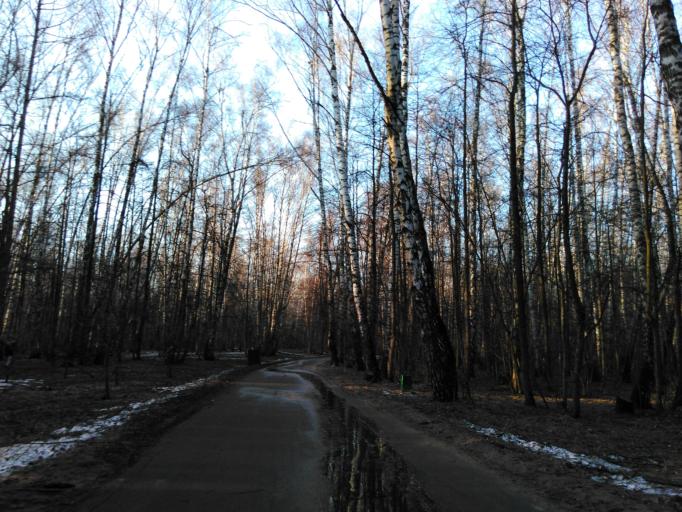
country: RU
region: Moscow
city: Zyuzino
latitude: 55.6421
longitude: 37.5665
